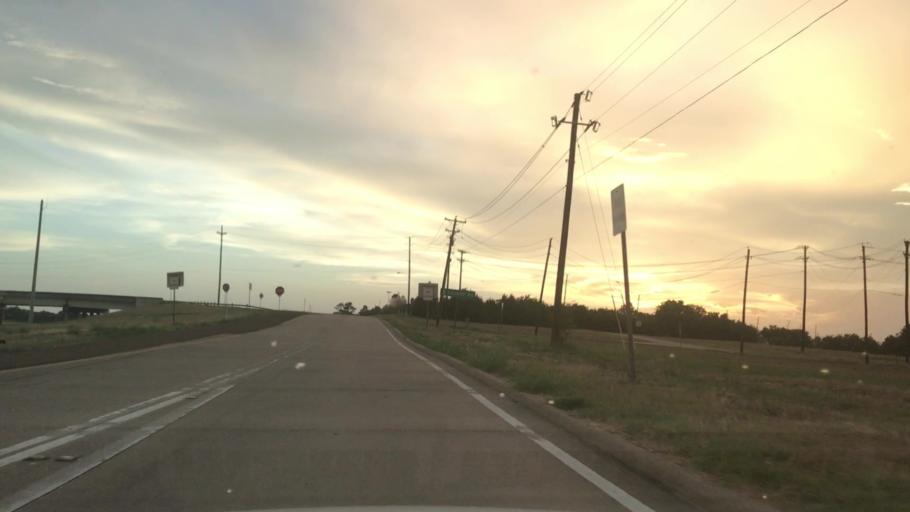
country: US
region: Texas
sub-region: Dallas County
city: Balch Springs
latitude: 32.7042
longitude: -96.5669
